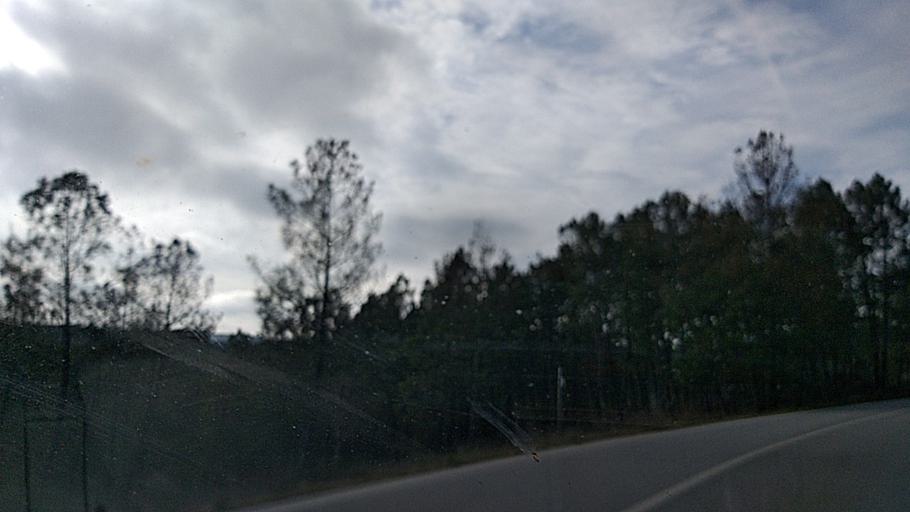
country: PT
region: Guarda
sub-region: Fornos de Algodres
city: Fornos de Algodres
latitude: 40.7131
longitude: -7.5634
